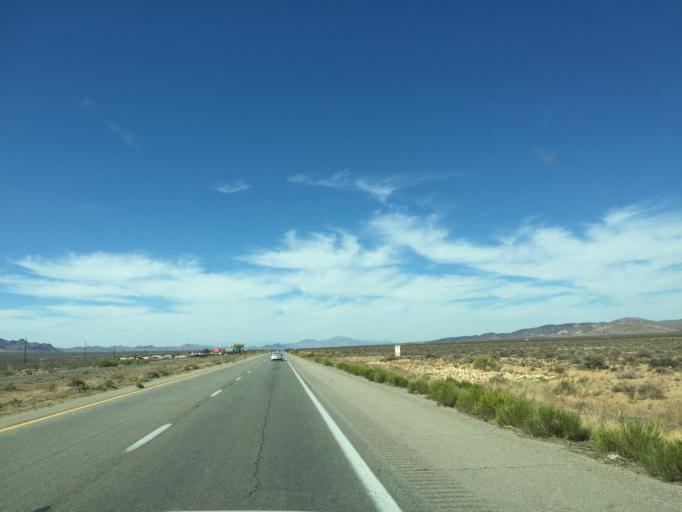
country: US
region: Arizona
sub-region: Mohave County
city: Dolan Springs
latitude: 35.5535
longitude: -114.3687
